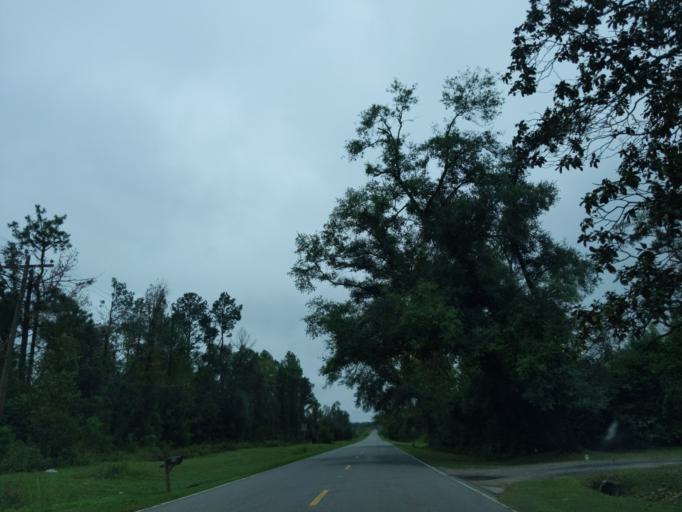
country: US
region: Florida
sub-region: Jackson County
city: Sneads
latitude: 30.7012
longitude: -84.9238
